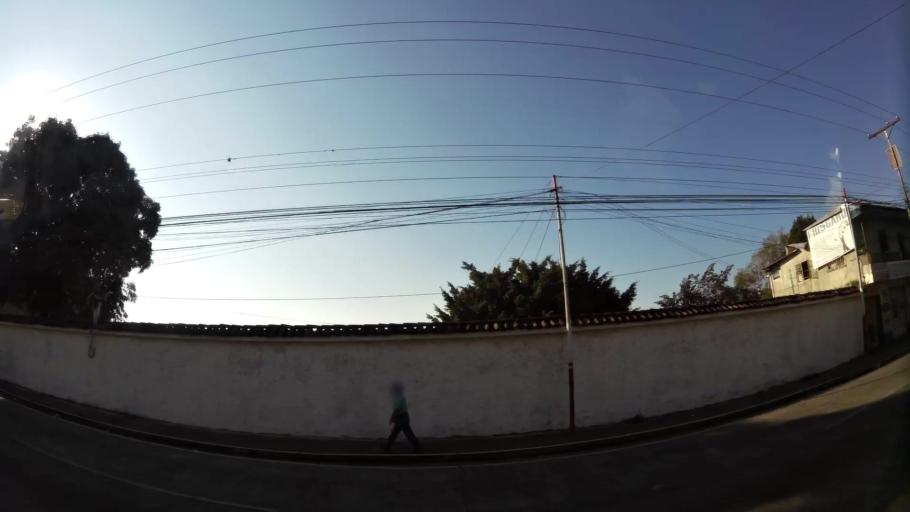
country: GT
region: Suchitepeque
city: Mazatenango
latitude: 14.5331
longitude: -91.5120
